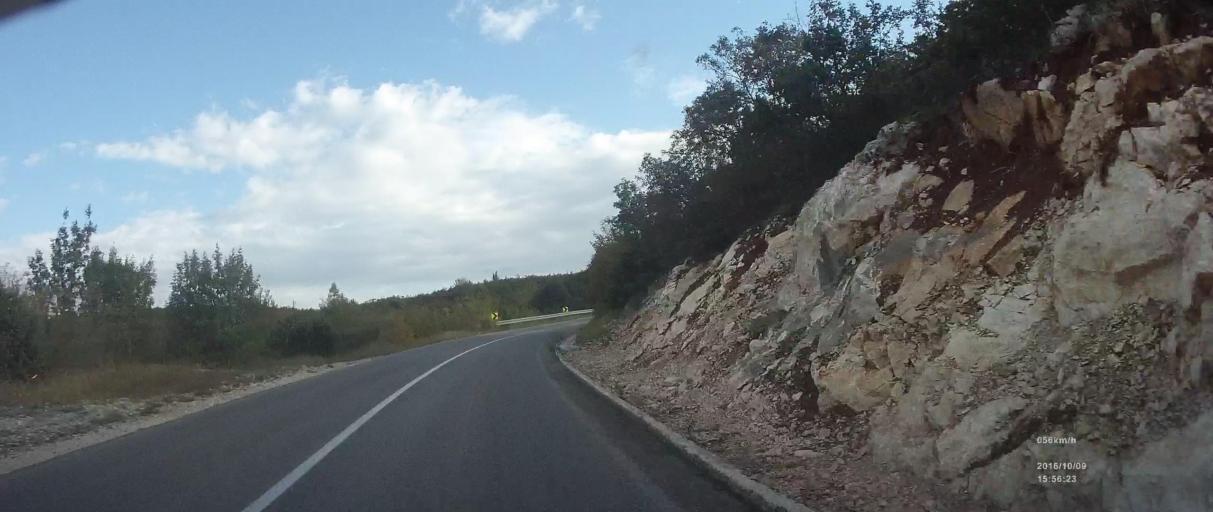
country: HR
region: Splitsko-Dalmatinska
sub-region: Grad Trogir
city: Trogir
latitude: 43.5788
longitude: 16.2334
